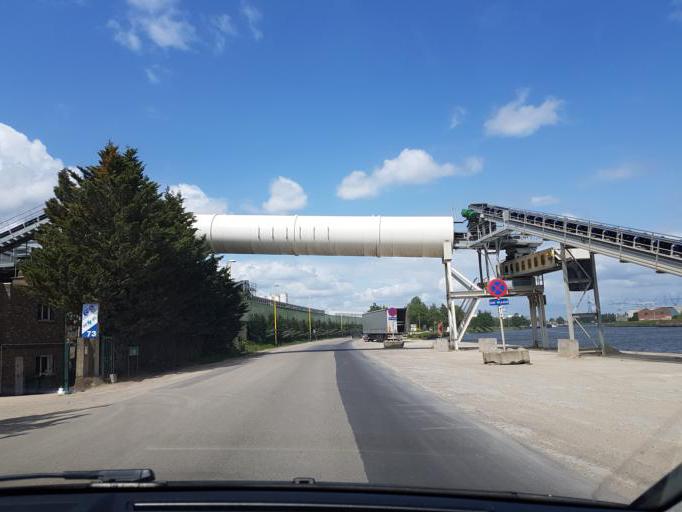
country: BE
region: Flanders
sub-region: Provincie Vlaams-Brabant
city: Vilvoorde
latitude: 50.9307
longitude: 4.4116
